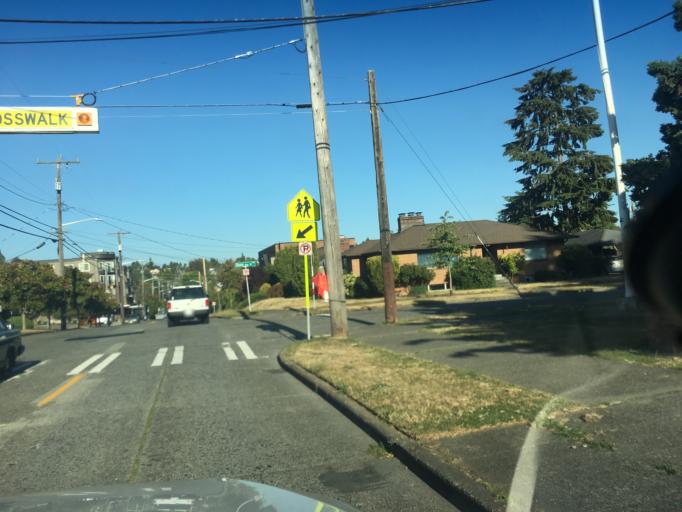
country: US
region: Washington
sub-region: King County
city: Shoreline
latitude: 47.6869
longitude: -122.3422
